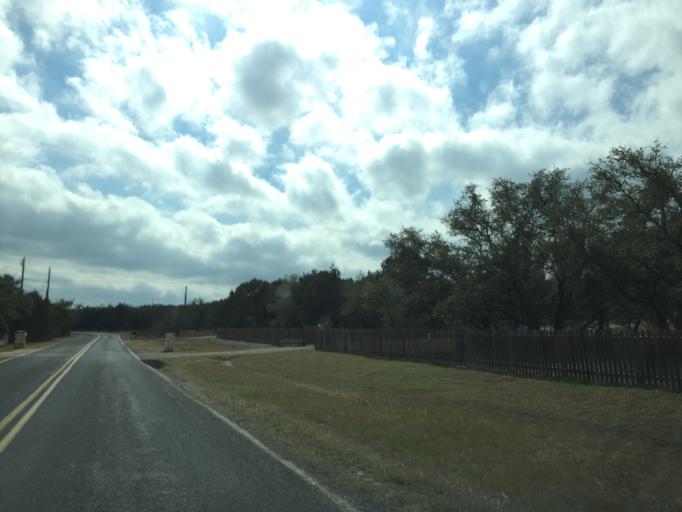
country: US
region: Texas
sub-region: Travis County
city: Briarcliff
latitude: 30.3771
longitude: -98.0937
